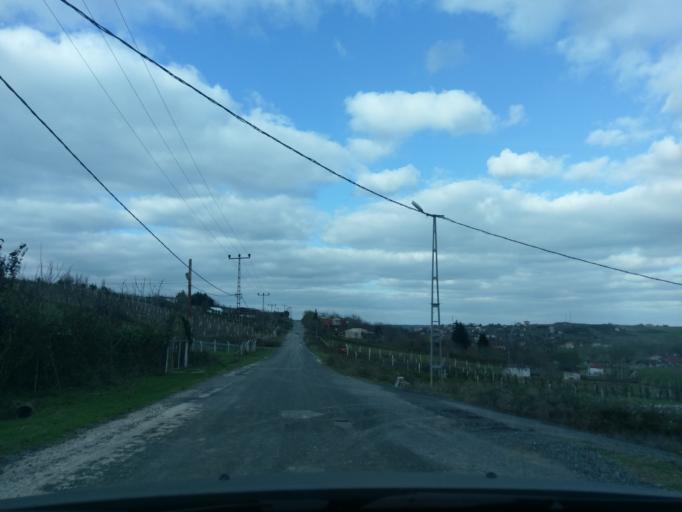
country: TR
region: Istanbul
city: Durusu
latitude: 41.2885
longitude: 28.6887
